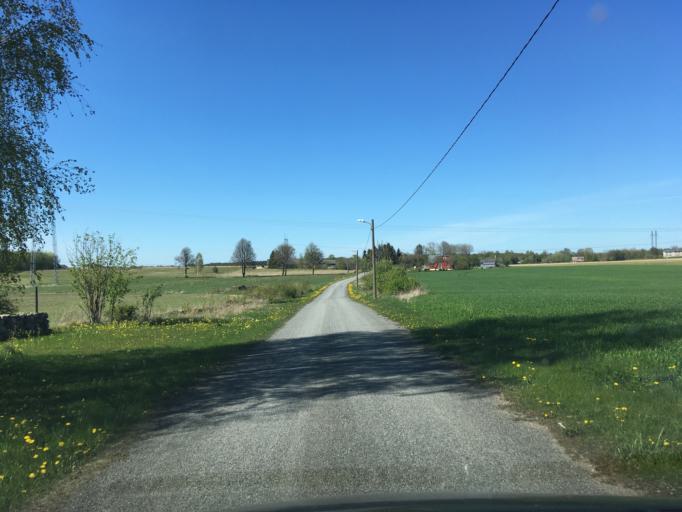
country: EE
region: Harju
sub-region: Raasiku vald
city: Arukula
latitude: 59.2673
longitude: 25.0947
